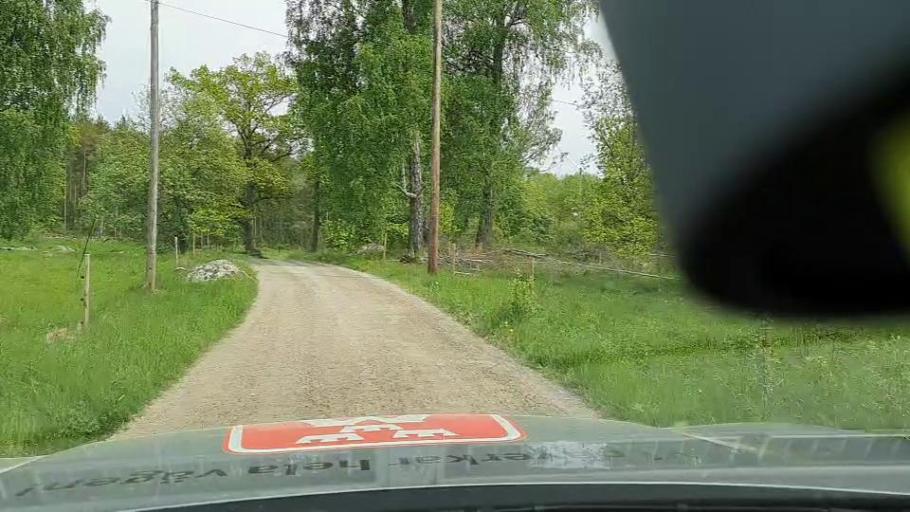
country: SE
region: Soedermanland
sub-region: Flens Kommun
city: Flen
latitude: 59.0421
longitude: 16.5738
